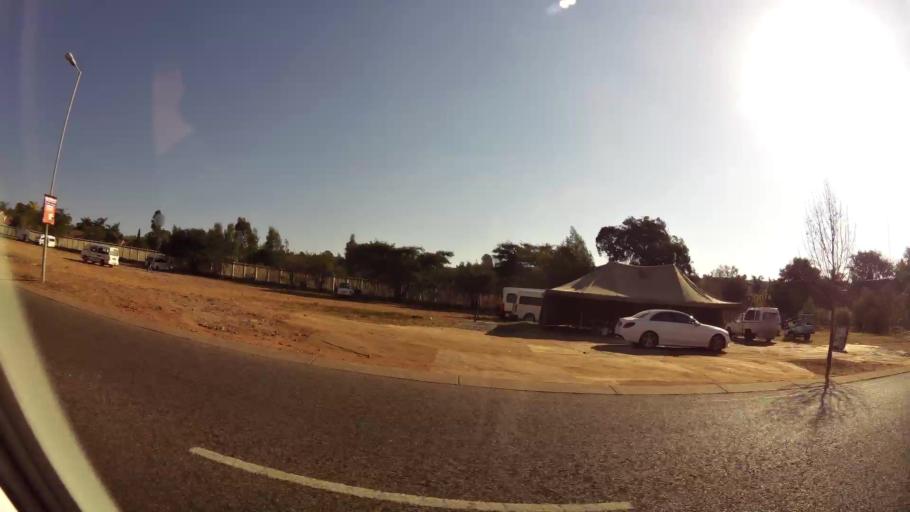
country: ZA
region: Gauteng
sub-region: City of Tshwane Metropolitan Municipality
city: Centurion
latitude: -25.8272
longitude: 28.2953
